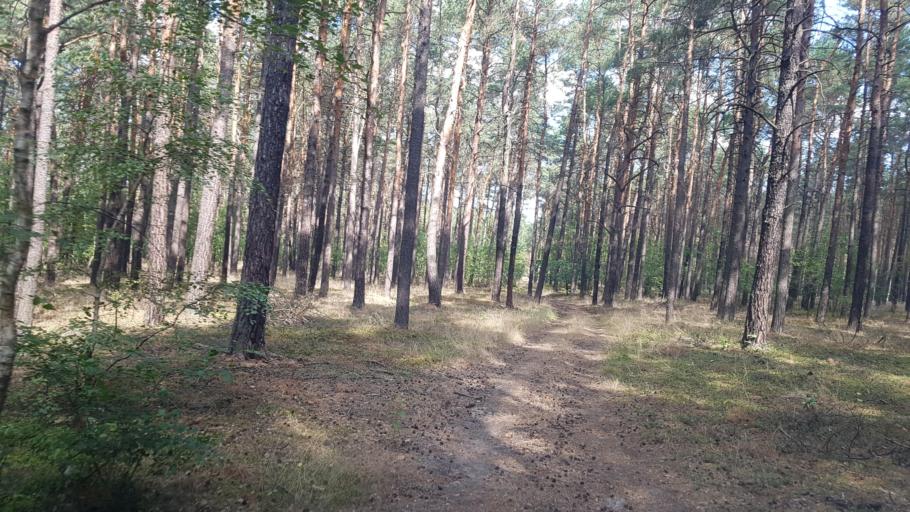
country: DE
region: Brandenburg
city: Finsterwalde
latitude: 51.6404
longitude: 13.7586
